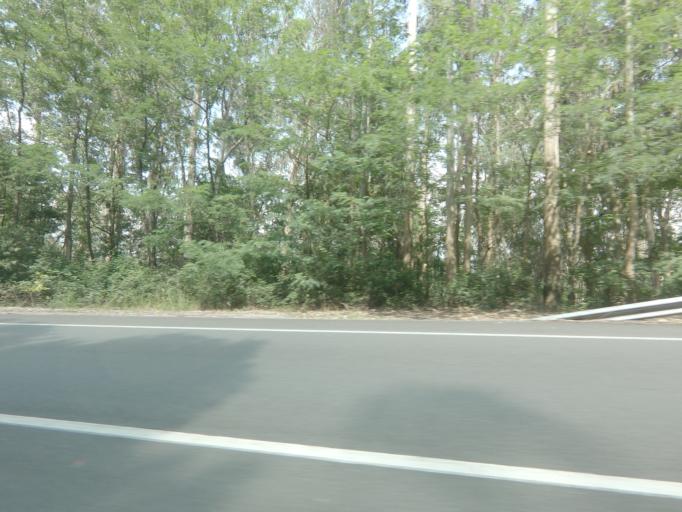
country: ES
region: Galicia
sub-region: Provincia de Pontevedra
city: Gondomar
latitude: 42.0947
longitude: -8.7565
